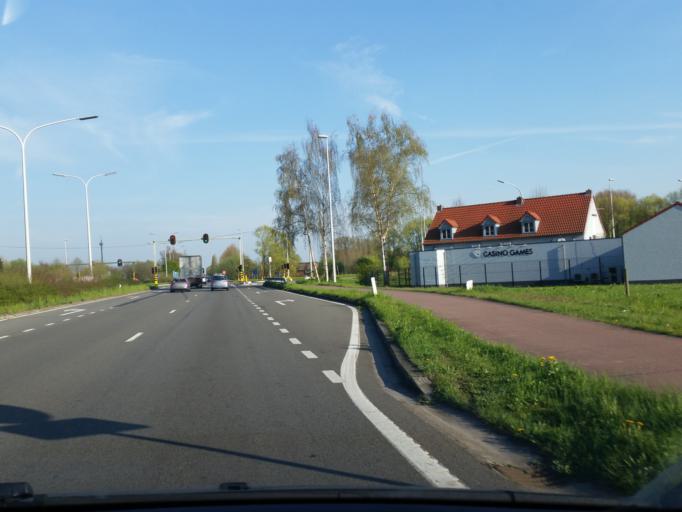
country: BE
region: Flanders
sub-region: Provincie Antwerpen
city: Bornem
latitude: 51.1065
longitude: 4.2343
